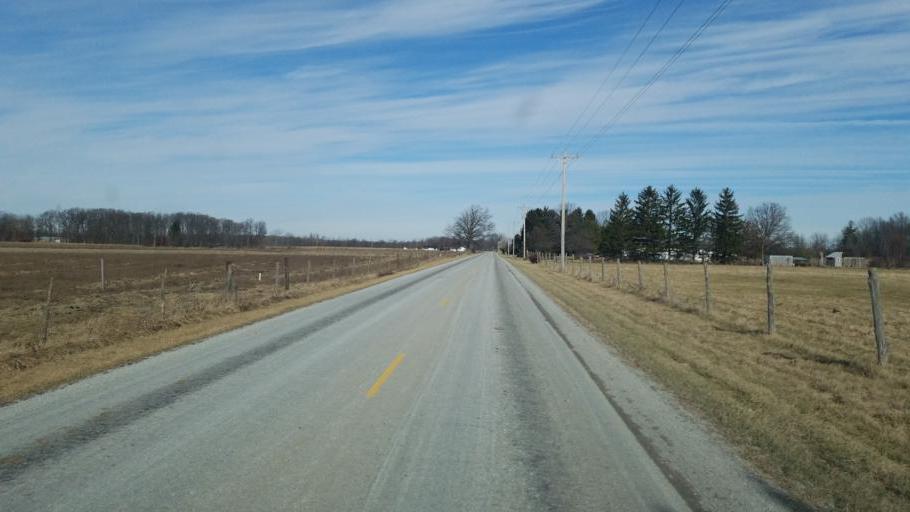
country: US
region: Ohio
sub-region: Hardin County
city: Kenton
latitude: 40.6090
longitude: -83.5031
